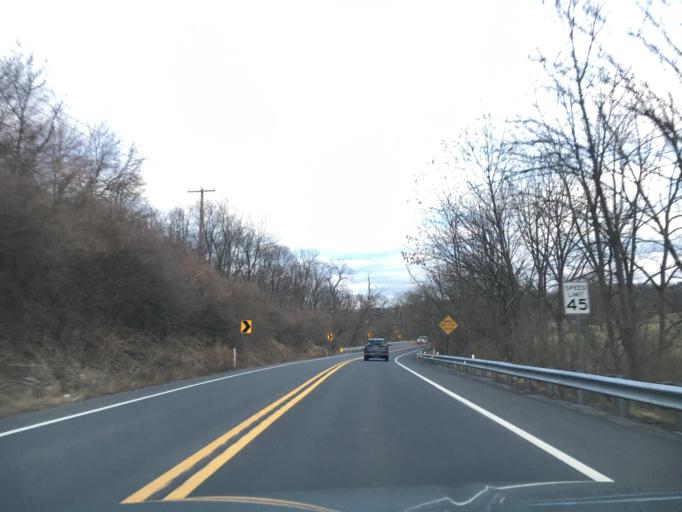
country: US
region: Pennsylvania
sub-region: Lehigh County
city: Schnecksville
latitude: 40.6785
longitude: -75.6476
